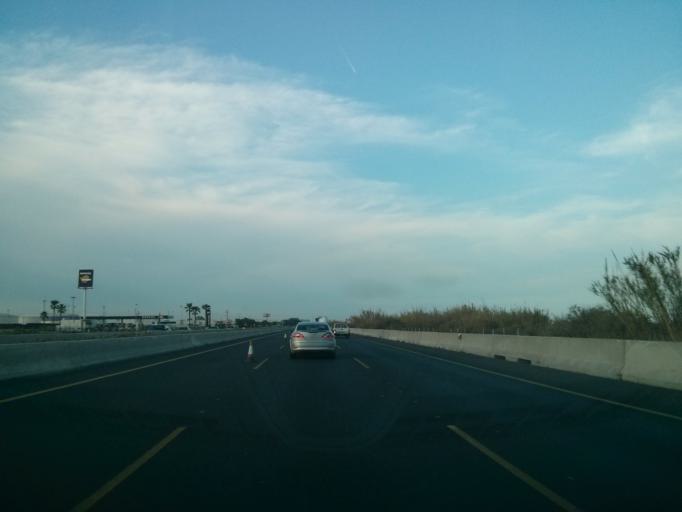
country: ES
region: Valencia
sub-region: Provincia de Valencia
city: Meliana
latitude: 39.5279
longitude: -0.3134
